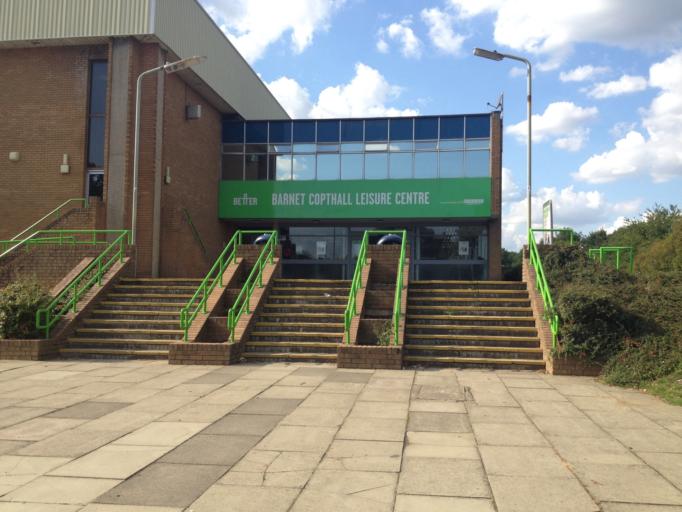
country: GB
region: England
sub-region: Greater London
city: Hendon
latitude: 51.6047
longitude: -0.2260
